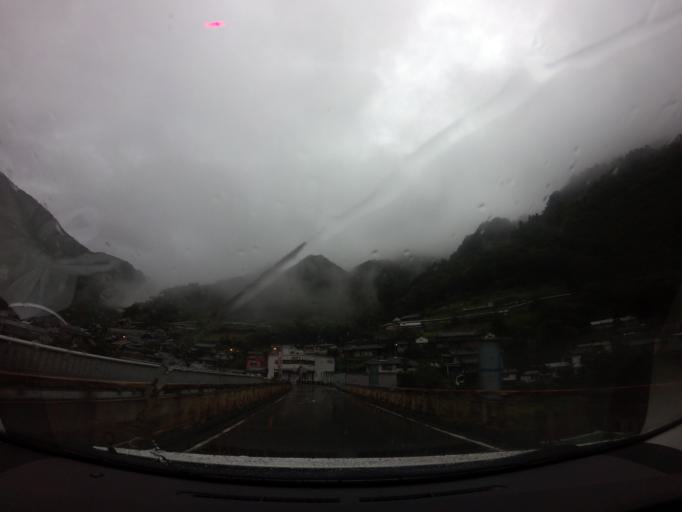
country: JP
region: Wakayama
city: Shingu
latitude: 33.9480
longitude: 135.8044
